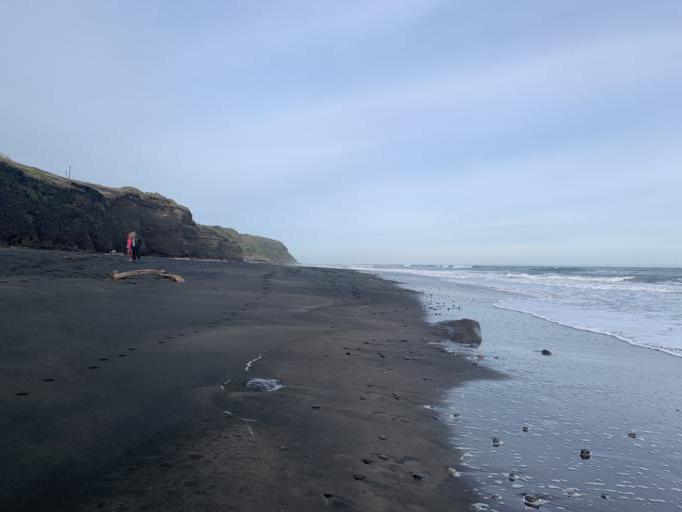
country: NZ
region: Taranaki
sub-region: South Taranaki District
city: Opunake
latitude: -39.5647
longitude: 174.0554
